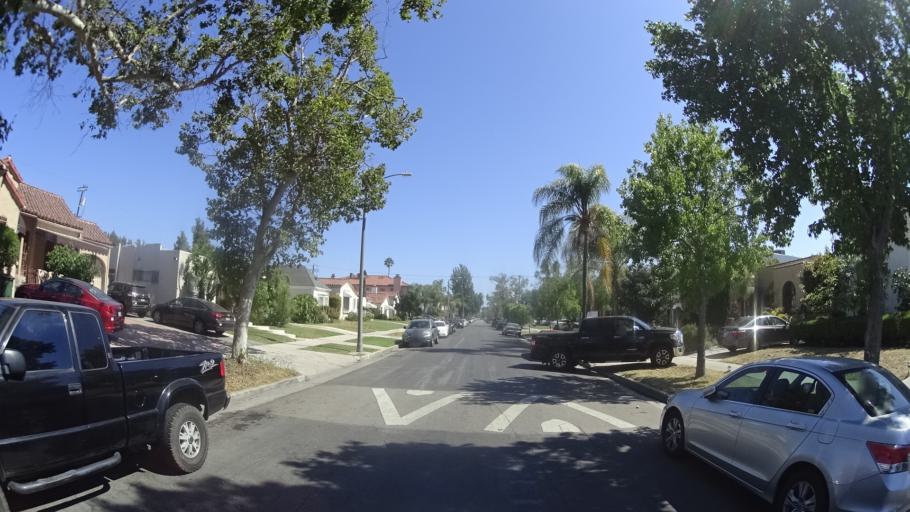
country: US
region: California
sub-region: Los Angeles County
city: West Hollywood
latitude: 34.0794
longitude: -118.3453
